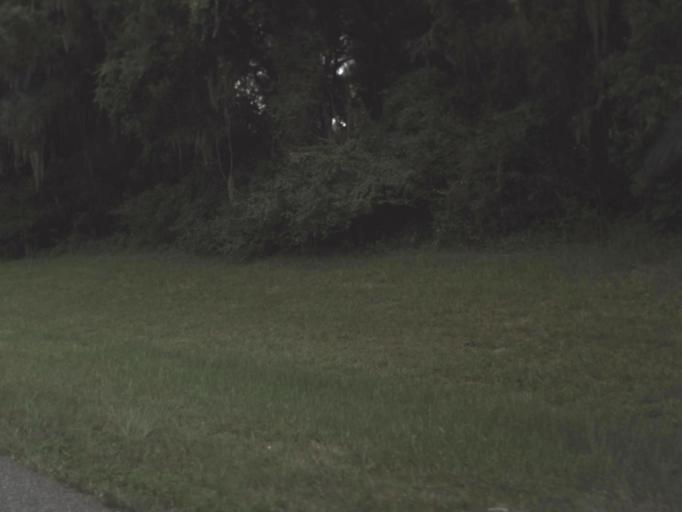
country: US
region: Florida
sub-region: Citrus County
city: Sugarmill Woods
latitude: 28.6668
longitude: -82.4718
